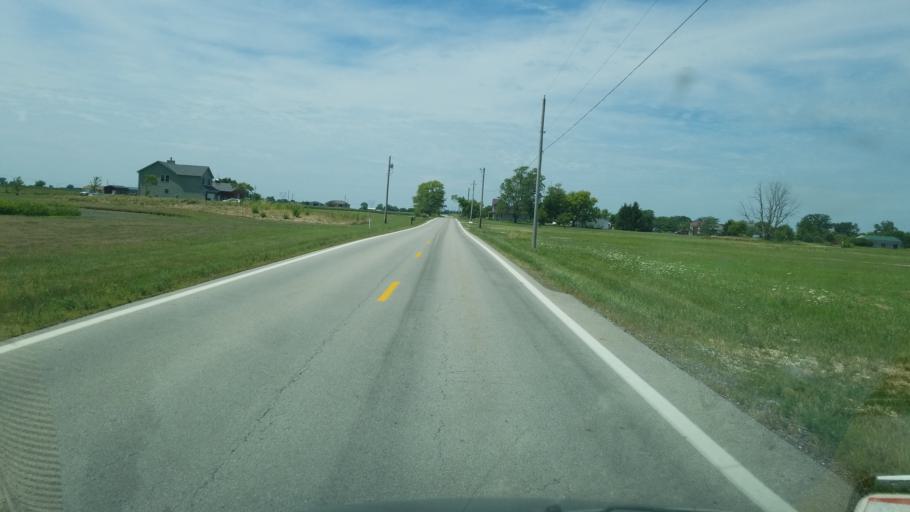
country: US
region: Ohio
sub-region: Madison County
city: West Jefferson
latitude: 39.8672
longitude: -83.2752
